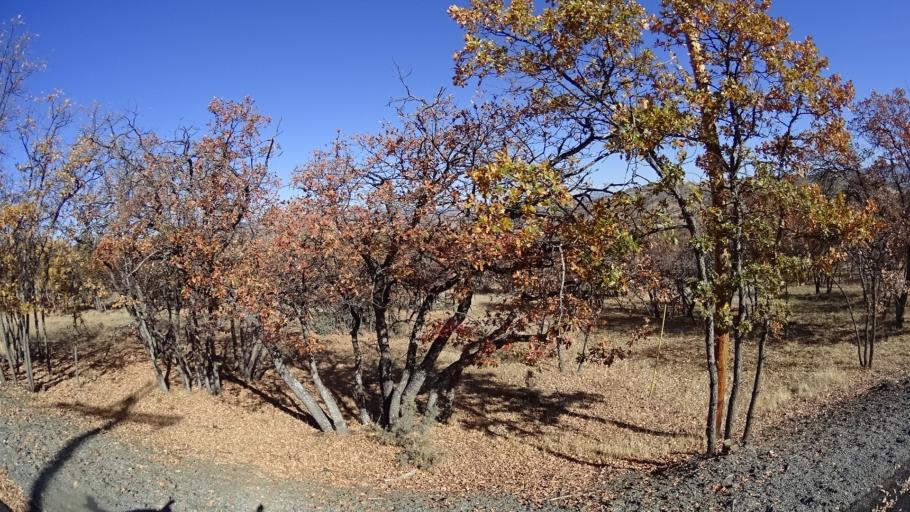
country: US
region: California
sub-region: Siskiyou County
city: Montague
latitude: 41.8779
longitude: -122.4887
